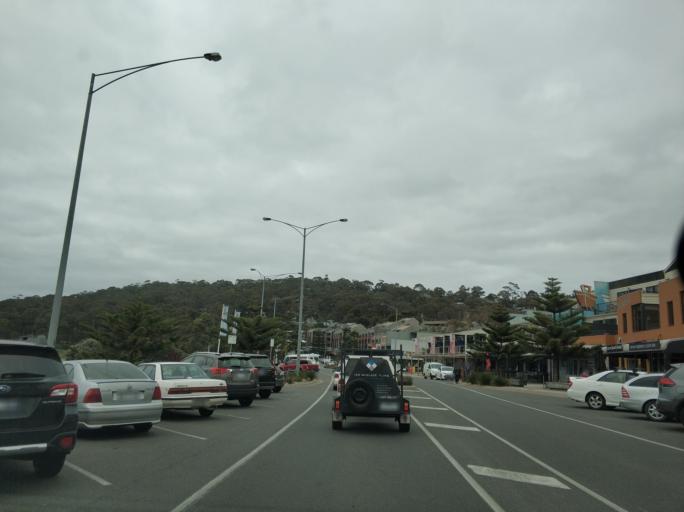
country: AU
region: Victoria
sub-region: Surf Coast
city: Anglesea
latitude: -38.5400
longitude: 143.9753
